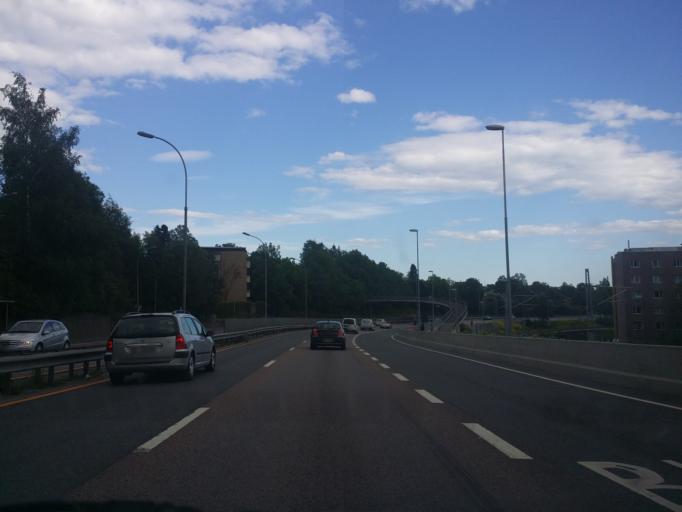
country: NO
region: Oslo
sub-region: Oslo
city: Oslo
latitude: 59.9518
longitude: 10.7739
